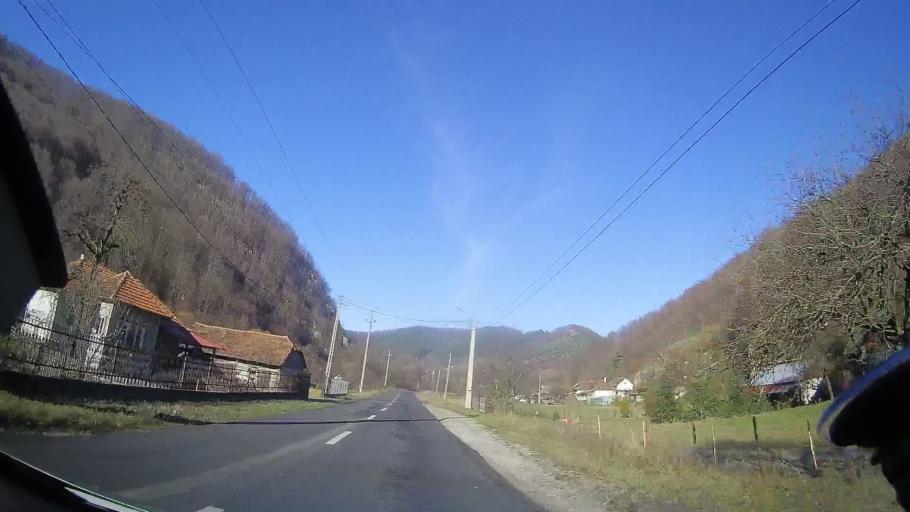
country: RO
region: Bihor
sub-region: Comuna Bulz
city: Bulz
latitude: 46.9179
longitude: 22.6553
